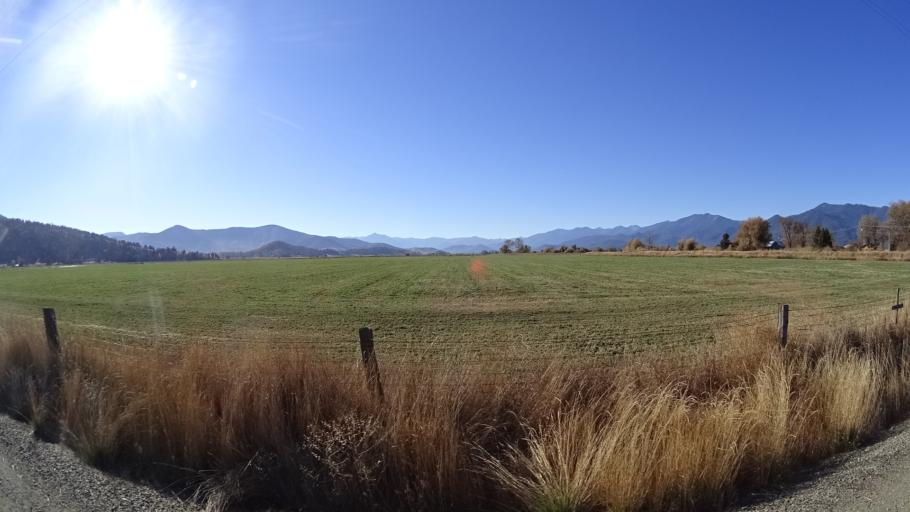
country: US
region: California
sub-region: Siskiyou County
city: Yreka
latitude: 41.5197
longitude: -122.8490
